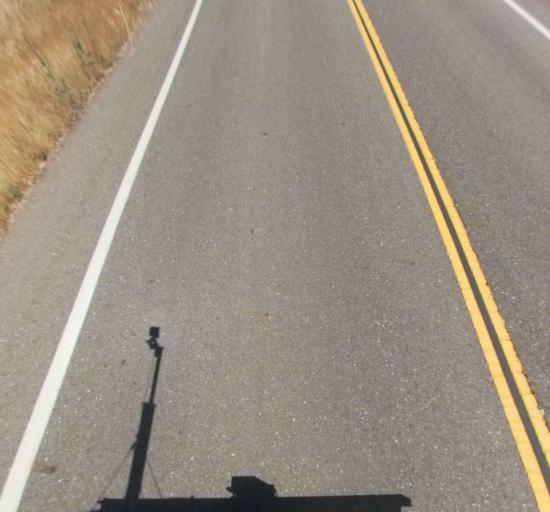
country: US
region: California
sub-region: Madera County
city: Fairmead
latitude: 37.0665
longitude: -120.1903
